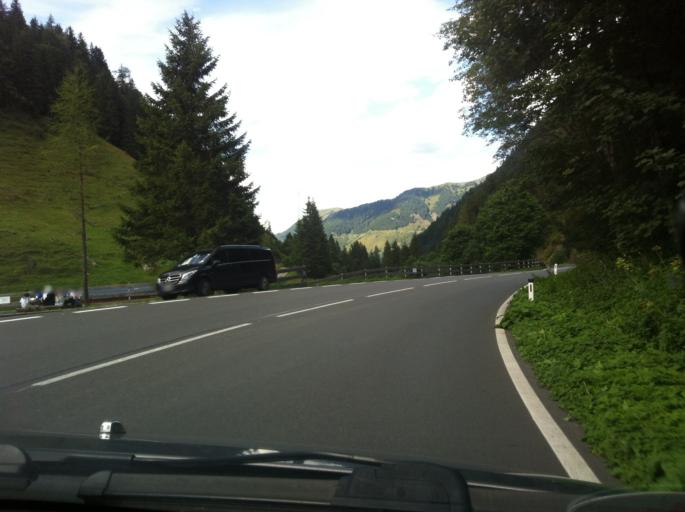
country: AT
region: Salzburg
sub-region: Politischer Bezirk Zell am See
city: Bruck an der Grossglocknerstrasse
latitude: 47.1745
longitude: 12.8170
